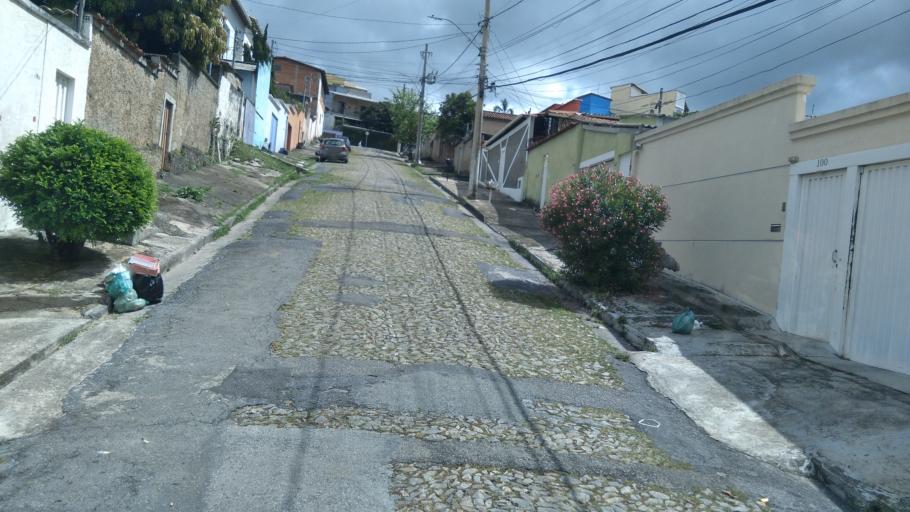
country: BR
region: Minas Gerais
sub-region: Belo Horizonte
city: Belo Horizonte
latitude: -19.8869
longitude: -43.9002
